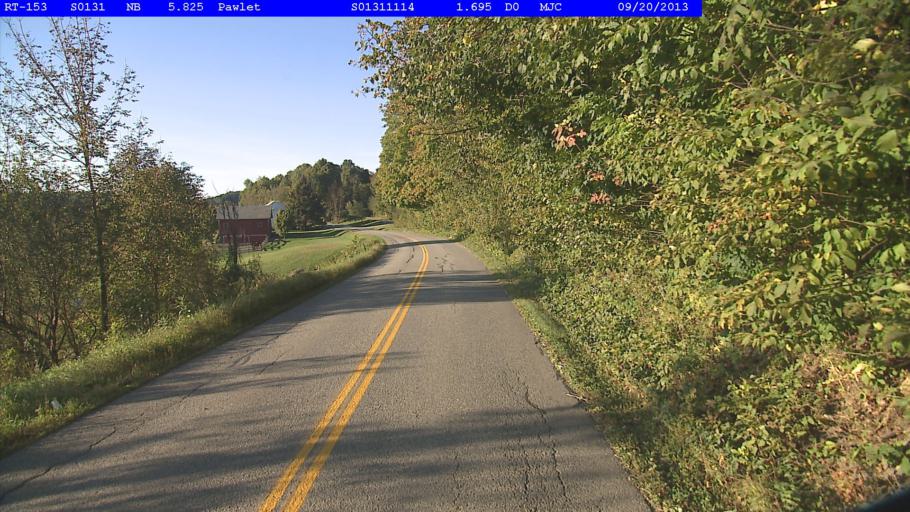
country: US
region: New York
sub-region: Washington County
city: Granville
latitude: 43.3384
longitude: -73.2434
